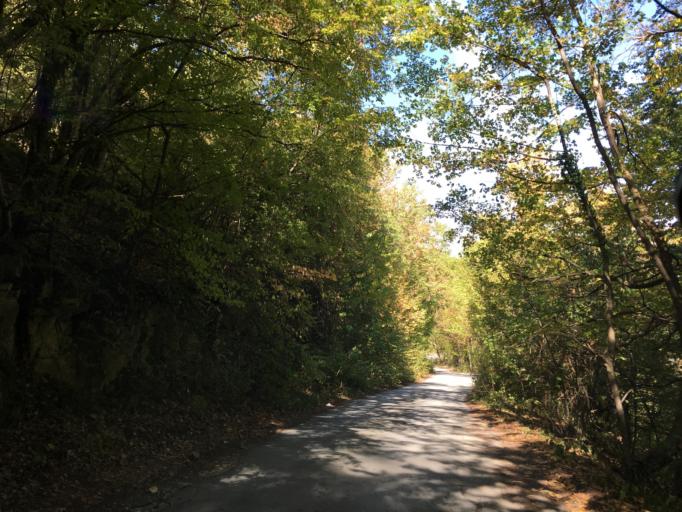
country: BG
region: Pazardzhik
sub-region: Obshtina Peshtera
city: Peshtera
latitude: 42.0055
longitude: 24.2796
